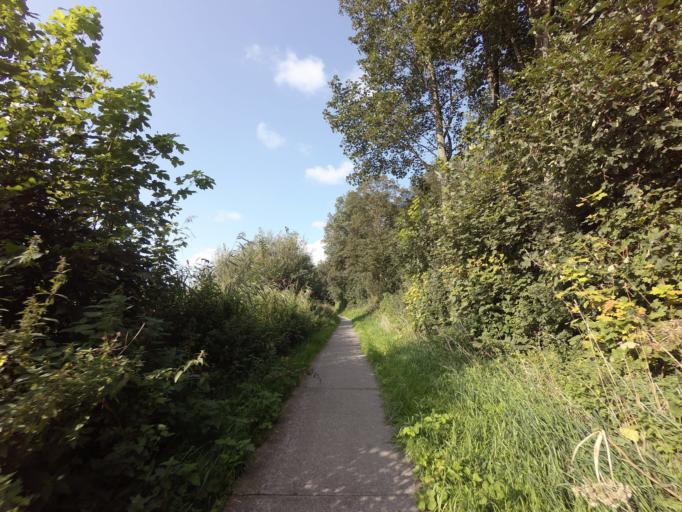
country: NL
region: Flevoland
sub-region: Gemeente Noordoostpolder
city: Ens
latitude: 52.6354
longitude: 5.7710
